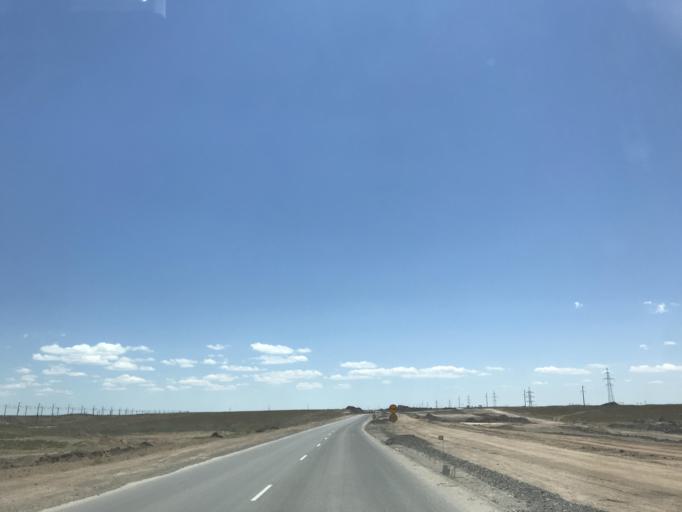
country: KZ
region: Almaty Oblysy
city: Ulken
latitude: 45.2556
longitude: 73.8067
